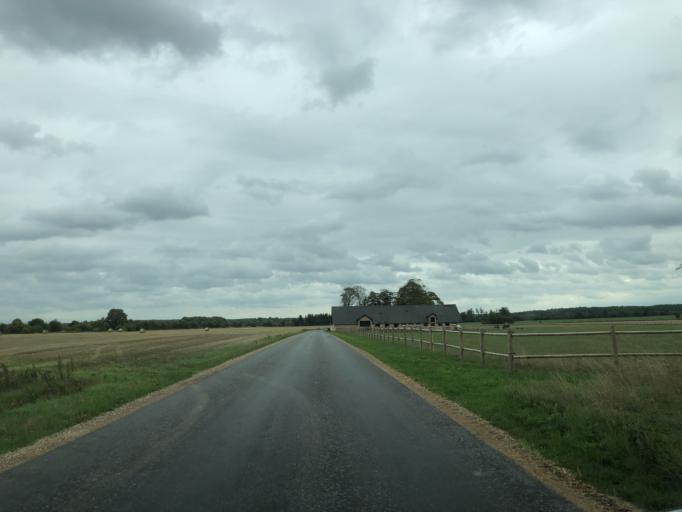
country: DK
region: Central Jutland
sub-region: Herning Kommune
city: Lind
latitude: 56.0906
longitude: 8.9297
